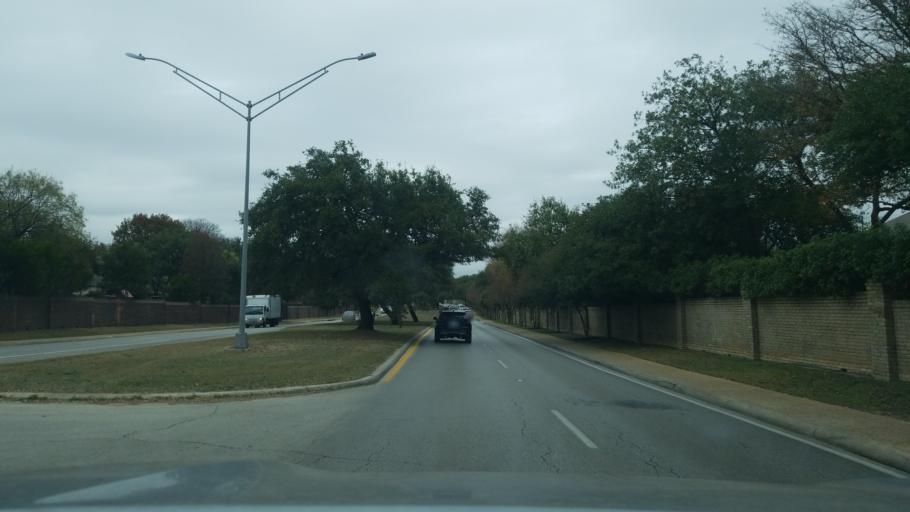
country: US
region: Texas
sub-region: Bexar County
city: Shavano Park
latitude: 29.5976
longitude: -98.5253
